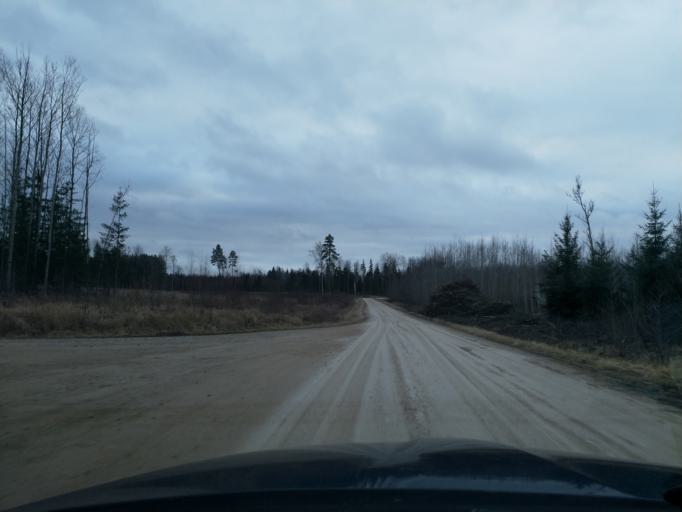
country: LV
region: Kuldigas Rajons
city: Kuldiga
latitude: 56.9150
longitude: 22.2697
